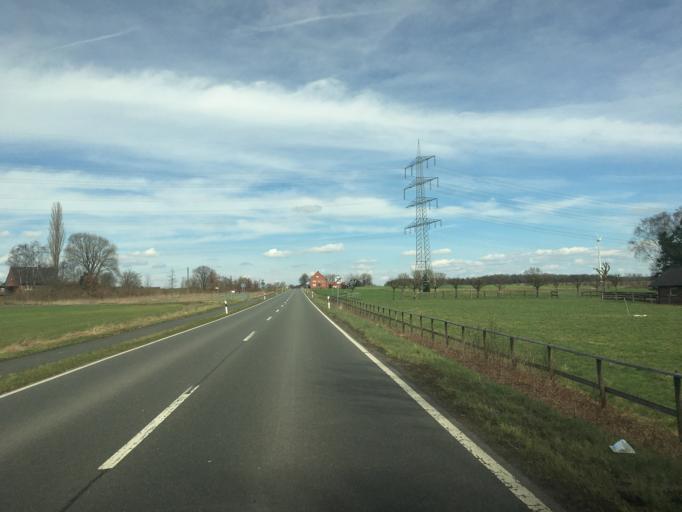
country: DE
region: North Rhine-Westphalia
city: Werne
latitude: 51.6893
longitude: 7.6319
